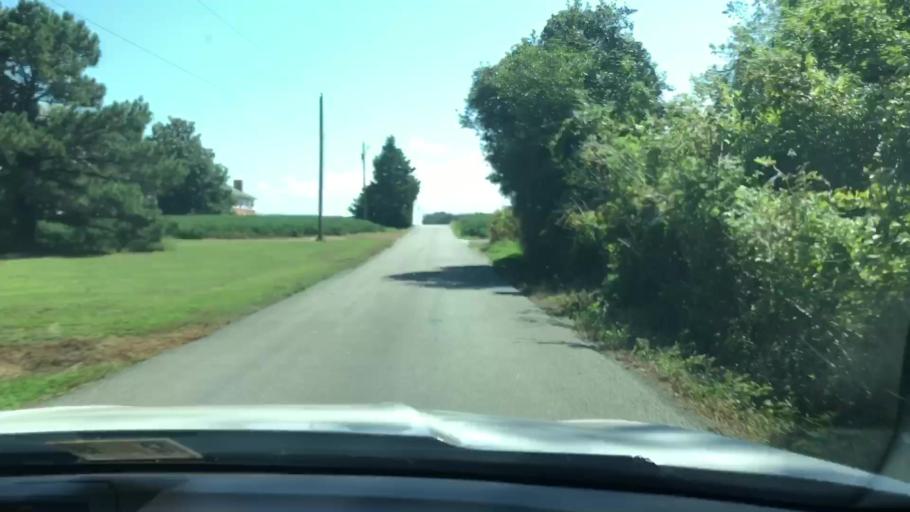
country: US
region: Virginia
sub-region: Charles City County
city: Charles City
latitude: 37.2532
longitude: -76.9561
